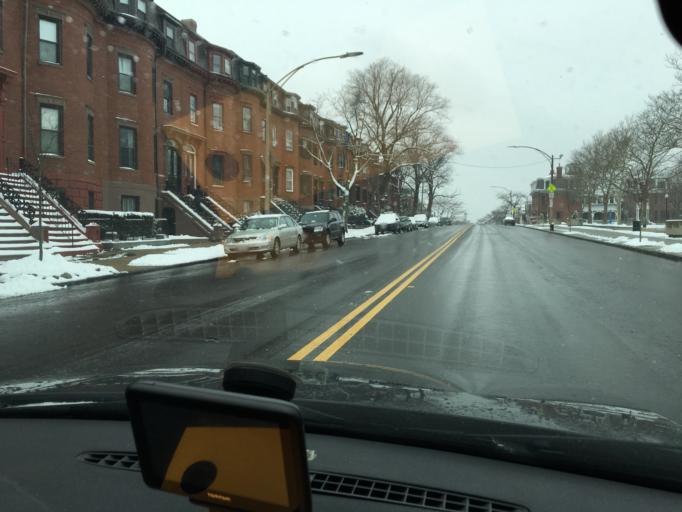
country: US
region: Massachusetts
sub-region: Suffolk County
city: South Boston
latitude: 42.3357
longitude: -71.0316
